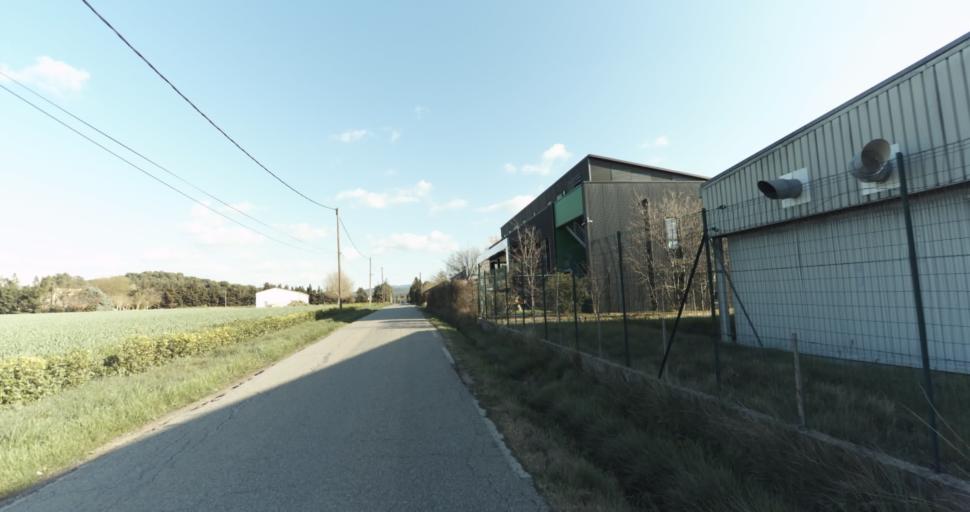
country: FR
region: Provence-Alpes-Cote d'Azur
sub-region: Departement des Bouches-du-Rhone
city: Bouc-Bel-Air
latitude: 43.4917
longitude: 5.3830
